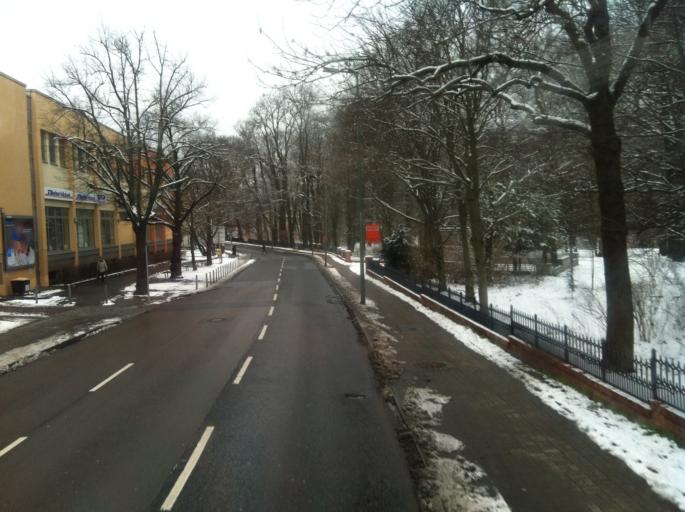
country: DE
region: Berlin
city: Buch
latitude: 52.6349
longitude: 13.4963
